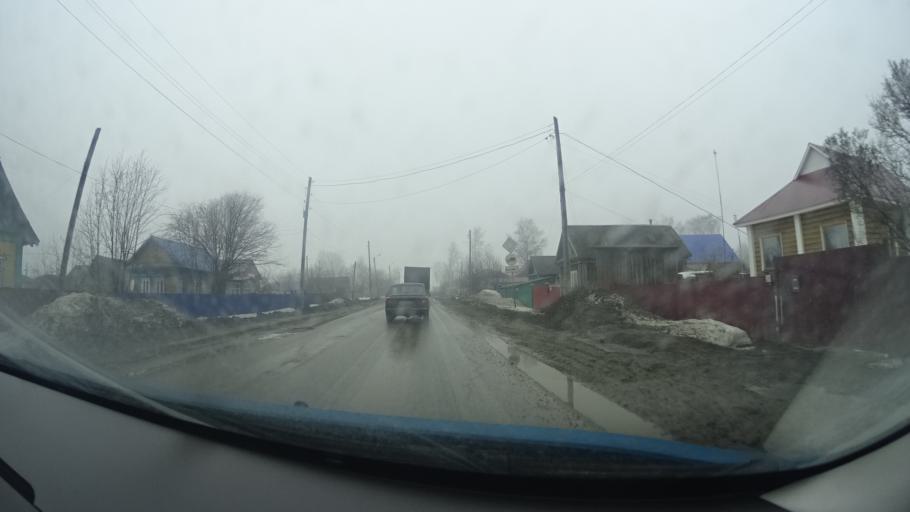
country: RU
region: Perm
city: Kuyeda
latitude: 56.4292
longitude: 55.5786
